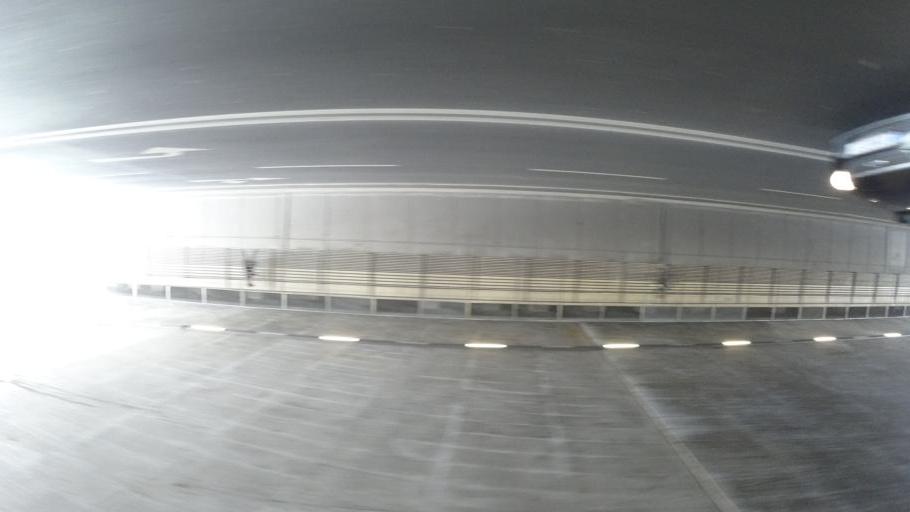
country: AT
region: Styria
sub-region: Graz Stadt
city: Wetzelsdorf
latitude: 47.0686
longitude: 15.4160
